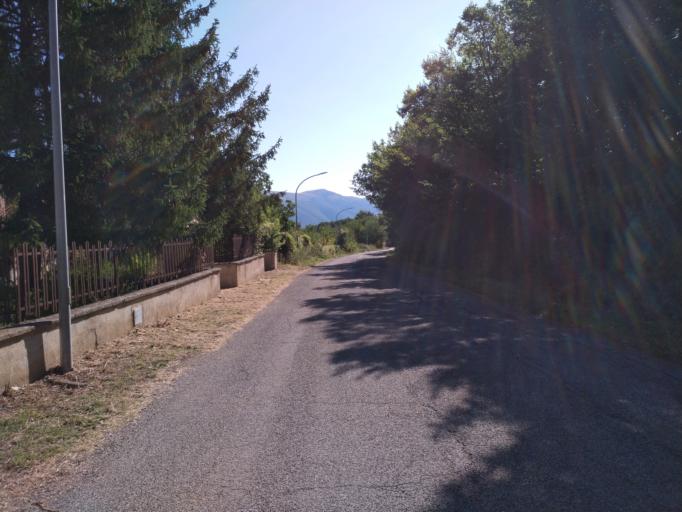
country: IT
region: Abruzzo
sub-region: Provincia dell' Aquila
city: Secinaro
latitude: 42.1797
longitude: 13.6654
